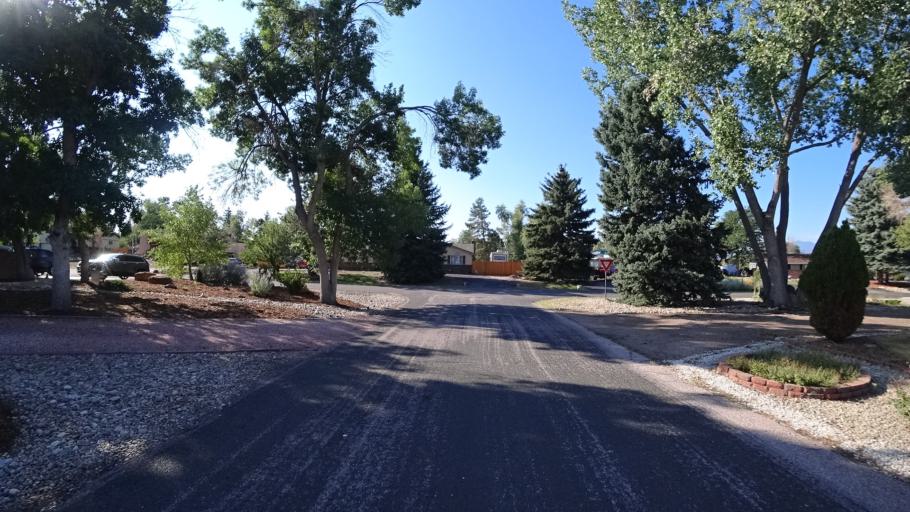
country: US
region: Colorado
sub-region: El Paso County
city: Air Force Academy
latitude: 38.9314
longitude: -104.7890
